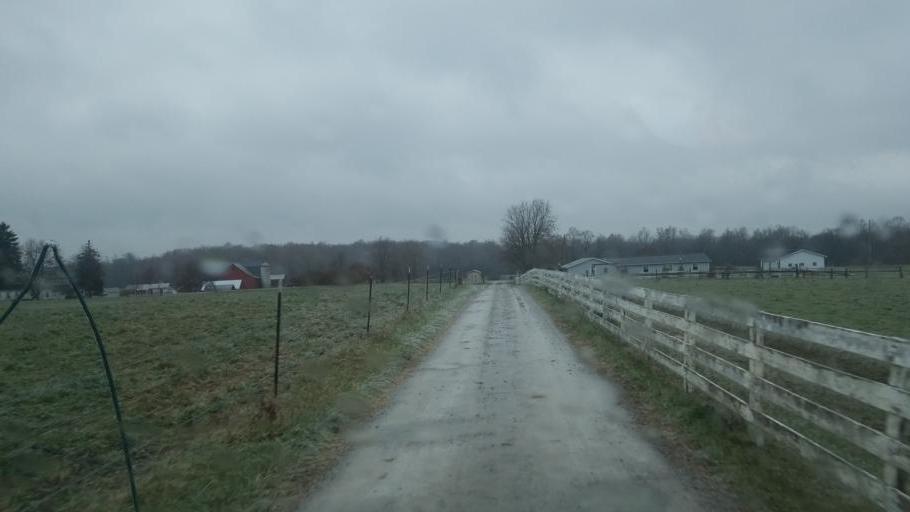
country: US
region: Ohio
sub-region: Richland County
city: Lexington
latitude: 40.5998
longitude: -82.6504
